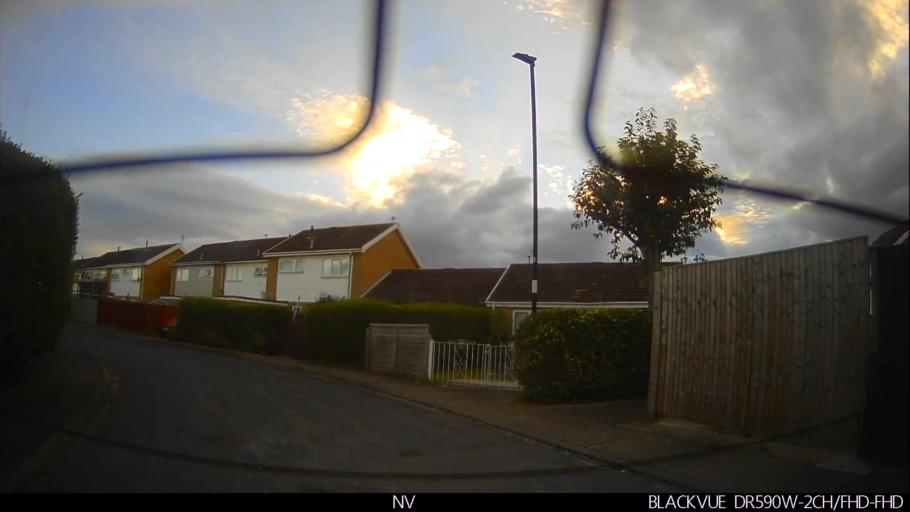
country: GB
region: England
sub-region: City of York
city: Copmanthorpe
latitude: 53.9411
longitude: -1.1317
